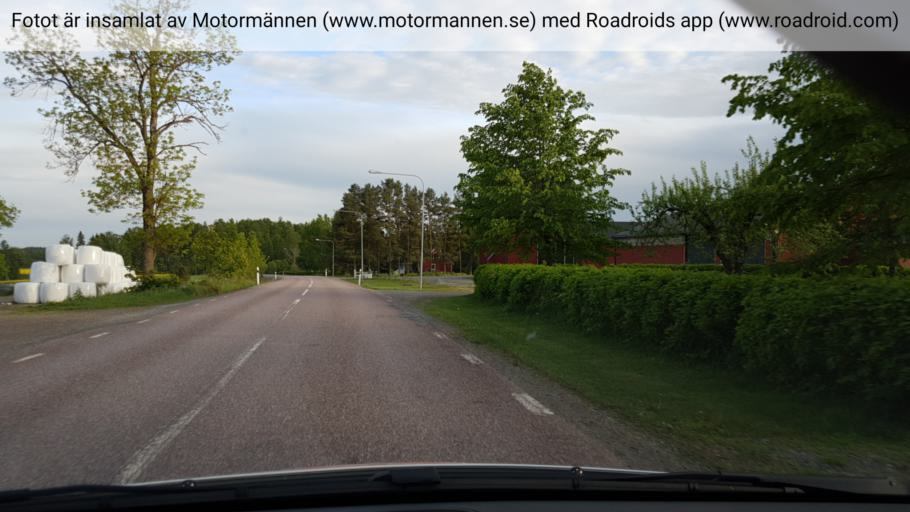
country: SE
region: Vaestmanland
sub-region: Kopings Kommun
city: Kolsva
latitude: 59.7204
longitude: 15.7918
